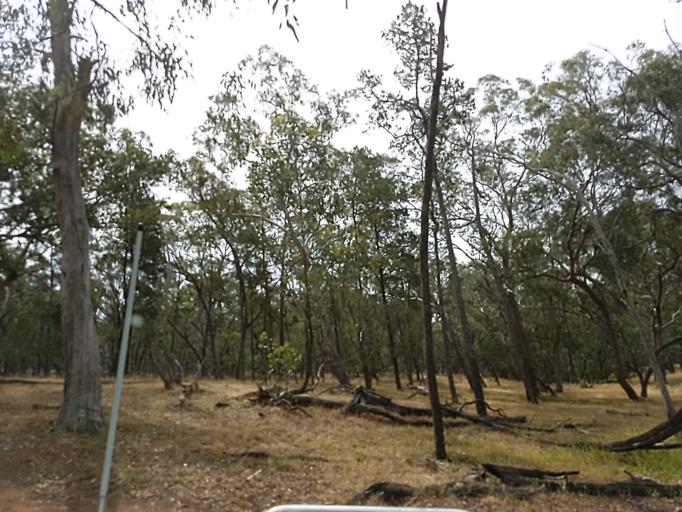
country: AU
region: New South Wales
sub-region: Snowy River
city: Jindabyne
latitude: -36.9651
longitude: 148.4133
